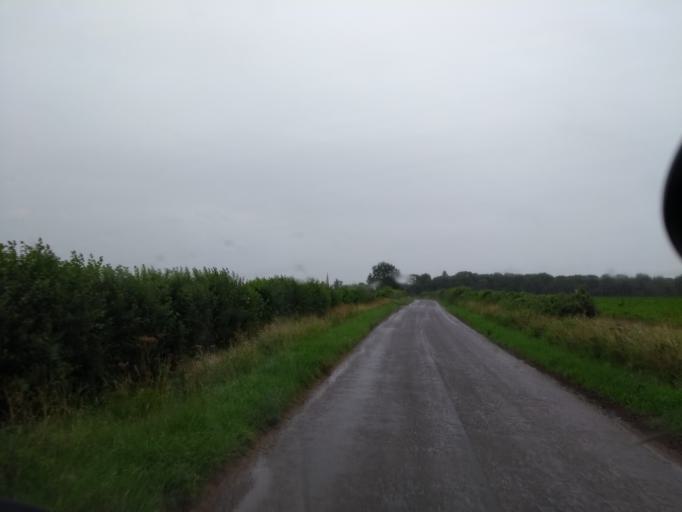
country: GB
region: England
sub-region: Somerset
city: Street
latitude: 51.0857
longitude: -2.6842
